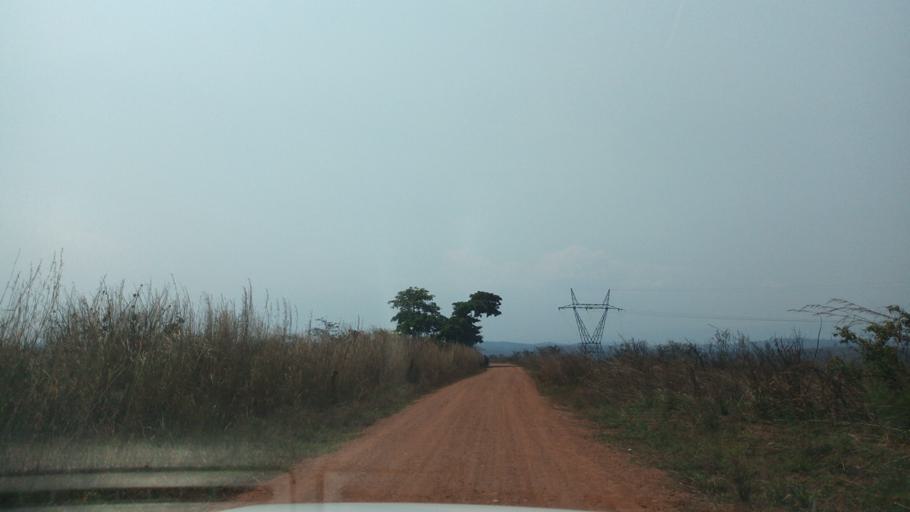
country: CD
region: Katanga
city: Kalemie
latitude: -5.7360
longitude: 29.0910
